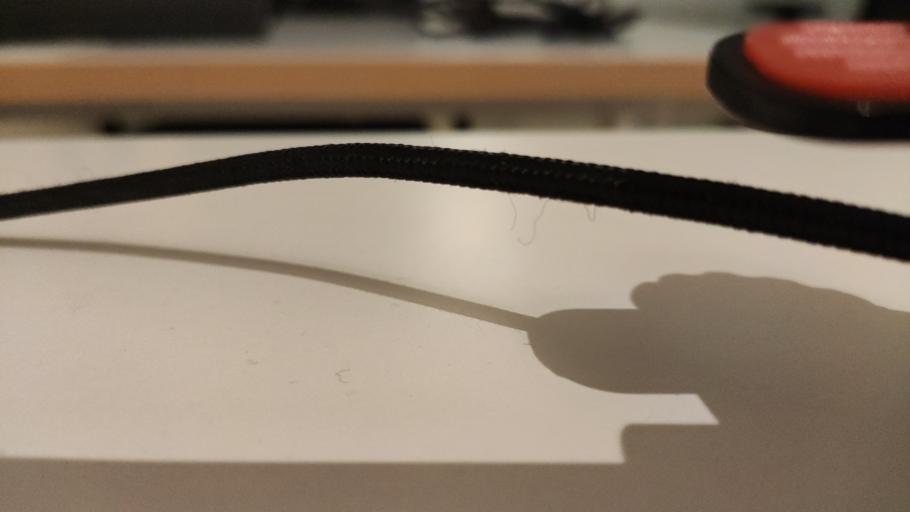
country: RU
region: Moskovskaya
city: Shaburnovo
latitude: 56.4276
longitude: 37.9528
